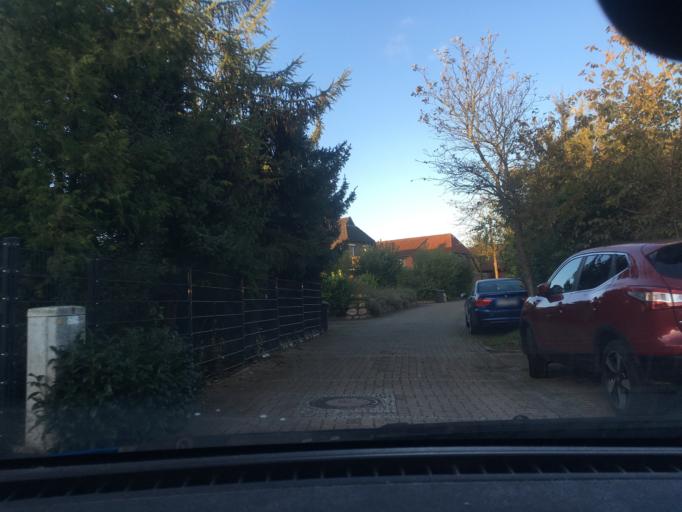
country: DE
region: Lower Saxony
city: Deutsch Evern
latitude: 53.2038
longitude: 10.4357
